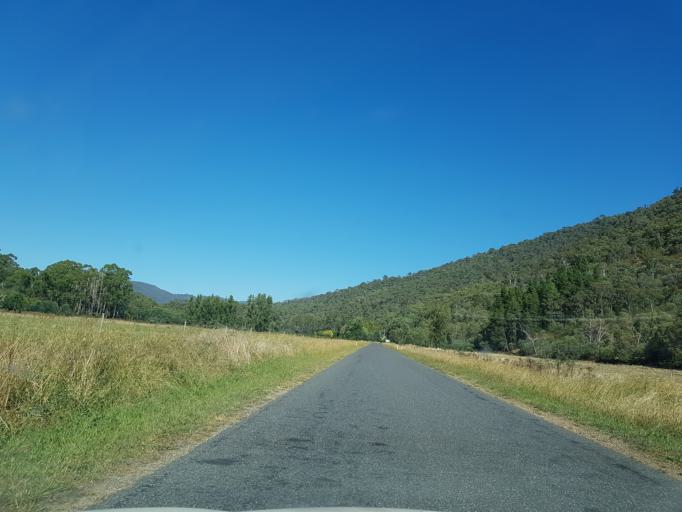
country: AU
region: Victoria
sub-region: Mansfield
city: Mansfield
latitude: -36.8667
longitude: 146.3771
